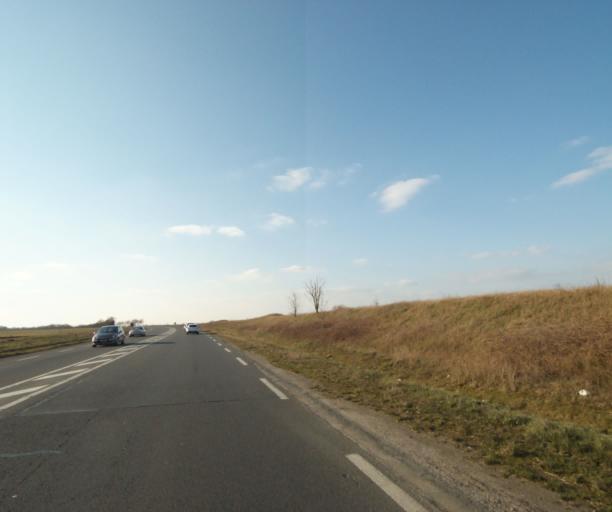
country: FR
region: Poitou-Charentes
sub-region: Departement des Deux-Sevres
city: Vouille
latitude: 46.3160
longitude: -0.3858
